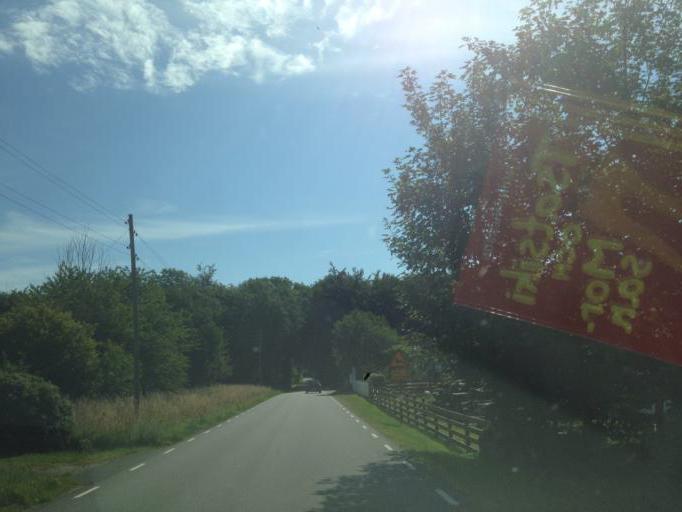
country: SE
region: Skane
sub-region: Simrishamns Kommun
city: Kivik
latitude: 55.6342
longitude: 14.1620
